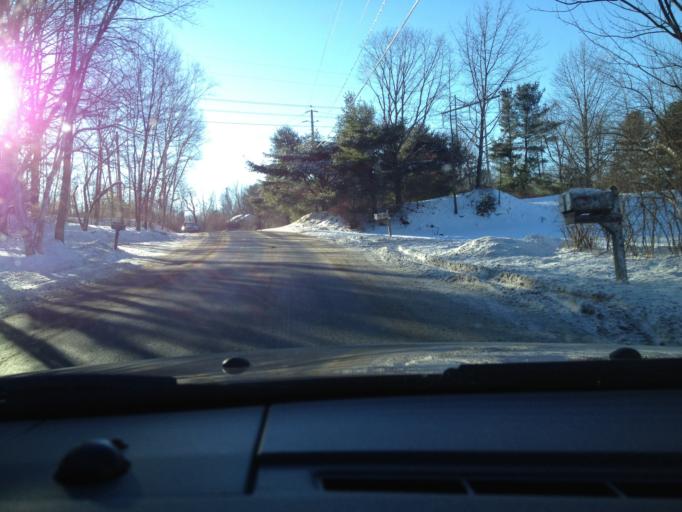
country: US
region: New York
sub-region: Rensselaer County
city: West Sand Lake
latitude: 42.6228
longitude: -73.5840
